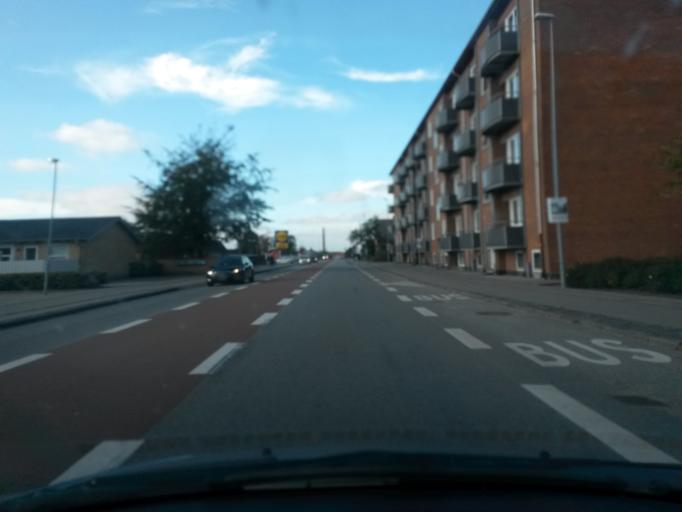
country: DK
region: Central Jutland
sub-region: Holstebro Kommune
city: Holstebro
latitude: 56.3494
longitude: 8.6258
